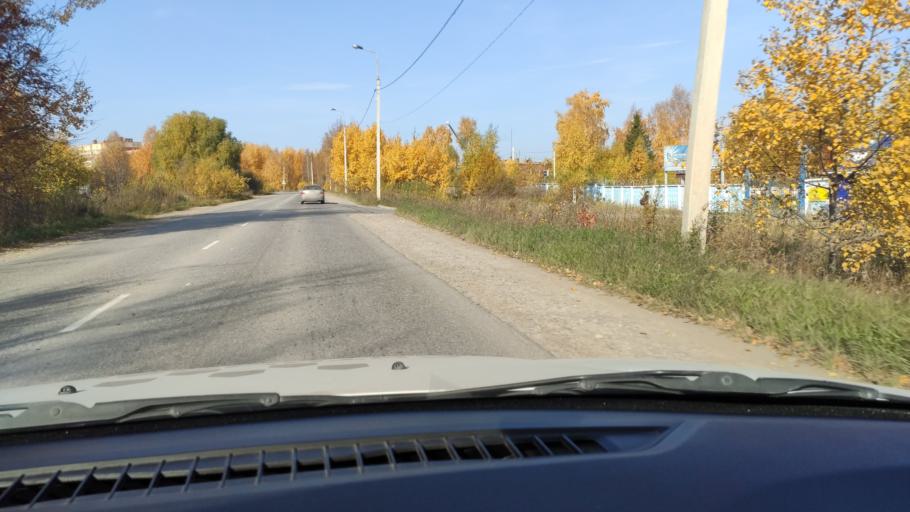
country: RU
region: Perm
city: Novyye Lyady
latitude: 58.0465
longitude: 56.5893
